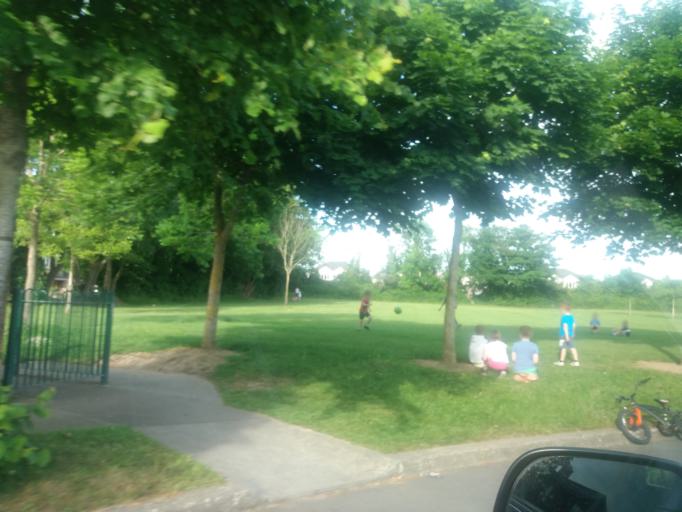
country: IE
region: Leinster
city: Hartstown
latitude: 53.3853
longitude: -6.4114
